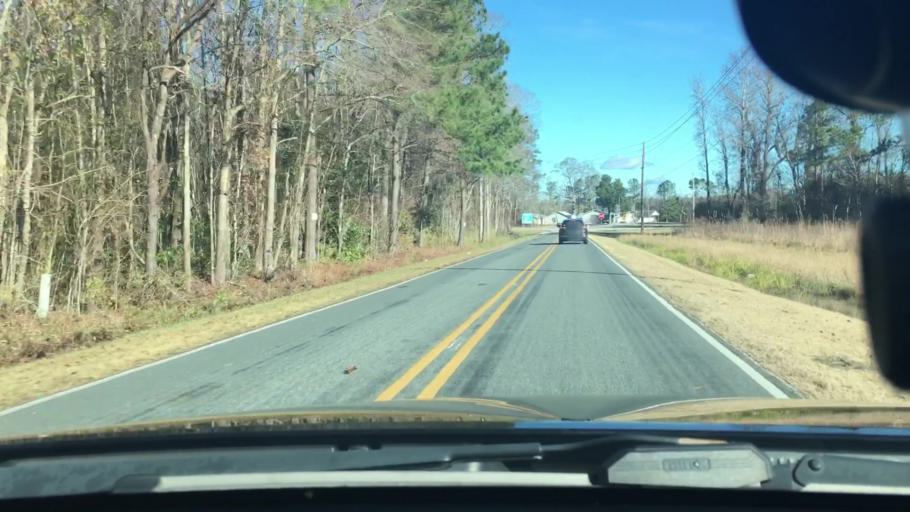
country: US
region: North Carolina
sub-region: Craven County
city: New Bern
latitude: 35.1936
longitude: -77.0547
